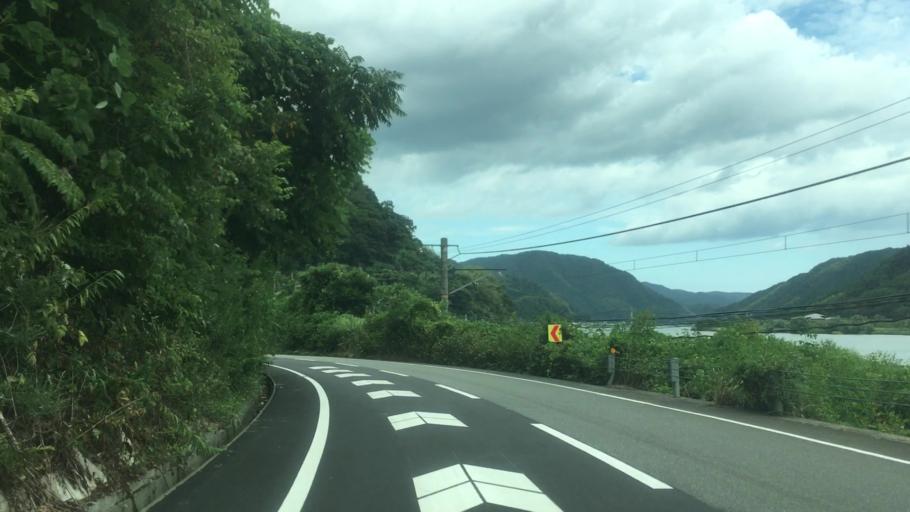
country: JP
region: Hyogo
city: Toyooka
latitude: 35.5797
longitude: 134.7999
